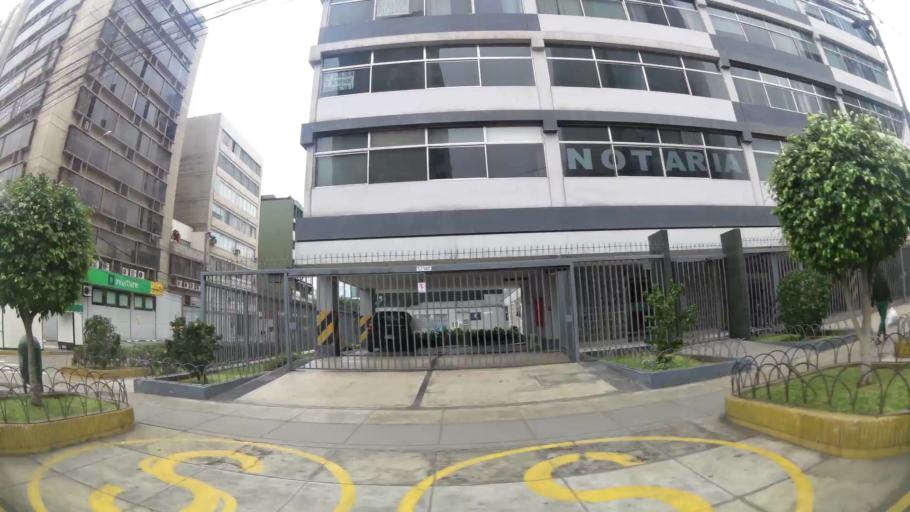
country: PE
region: Lima
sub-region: Lima
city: San Isidro
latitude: -12.0970
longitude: -77.0224
